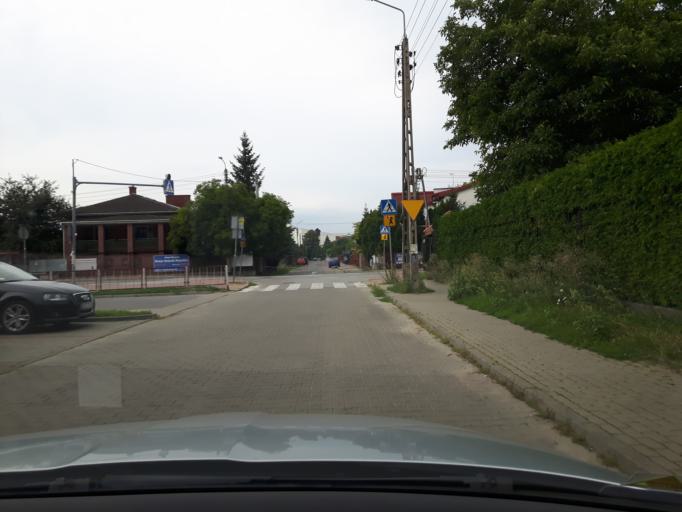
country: PL
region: Masovian Voivodeship
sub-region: Powiat wolominski
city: Zabki
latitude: 52.2944
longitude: 21.1045
